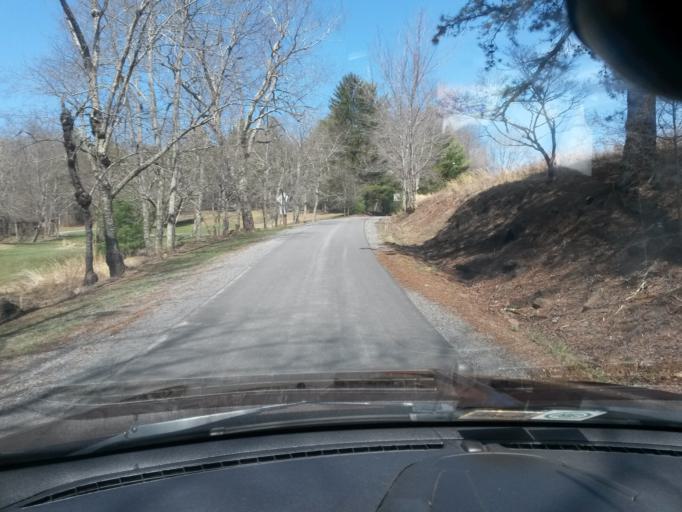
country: US
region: West Virginia
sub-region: Greenbrier County
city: Ronceverte
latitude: 37.6213
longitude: -80.3533
